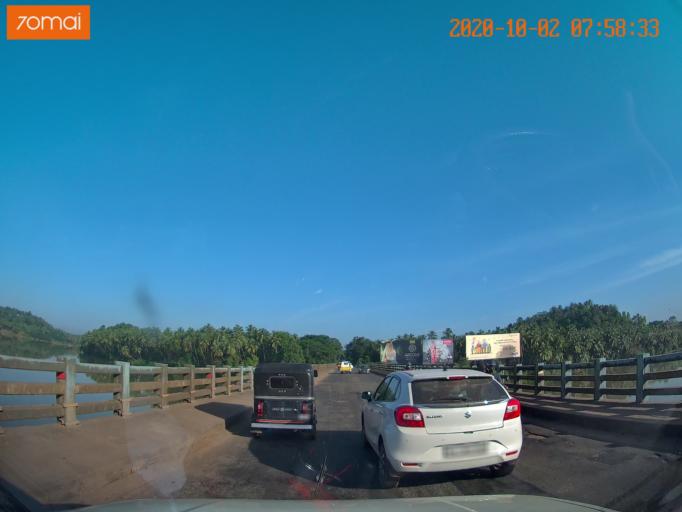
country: IN
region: Kerala
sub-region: Kozhikode
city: Ferokh
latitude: 11.2049
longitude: 75.8646
